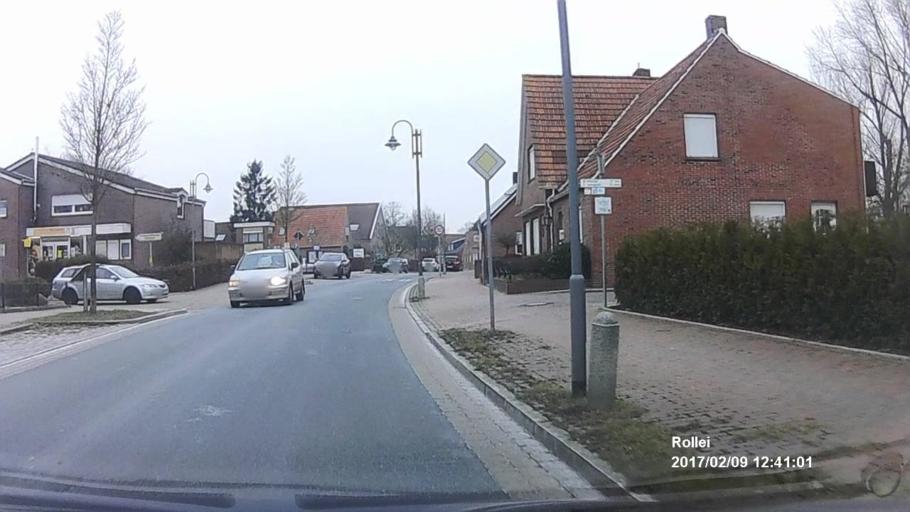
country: DE
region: Lower Saxony
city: Leer
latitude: 53.2221
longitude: 7.4149
